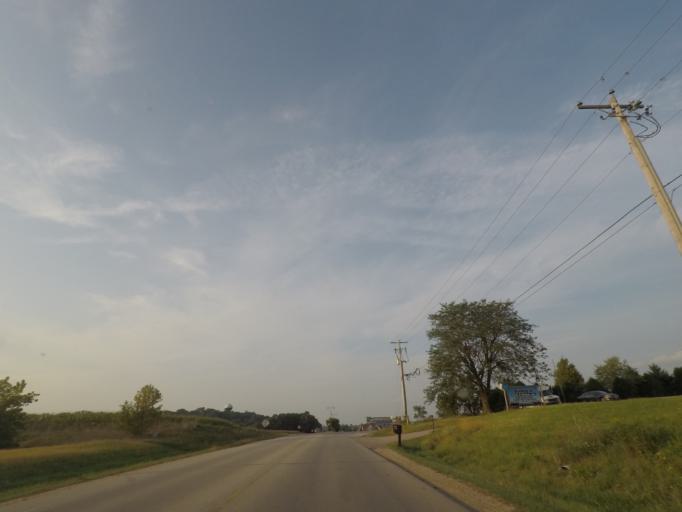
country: US
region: Wisconsin
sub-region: Dane County
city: Cottage Grove
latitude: 43.1011
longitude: -89.1995
